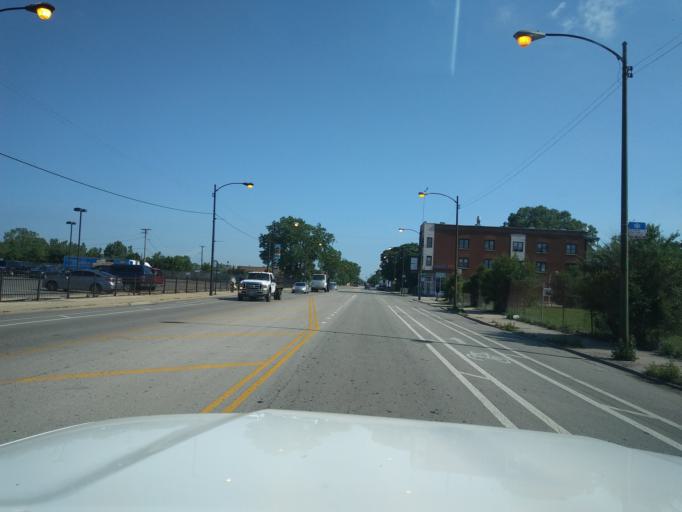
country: US
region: Illinois
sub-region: Cook County
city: Chicago
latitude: 41.8100
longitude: -87.6456
